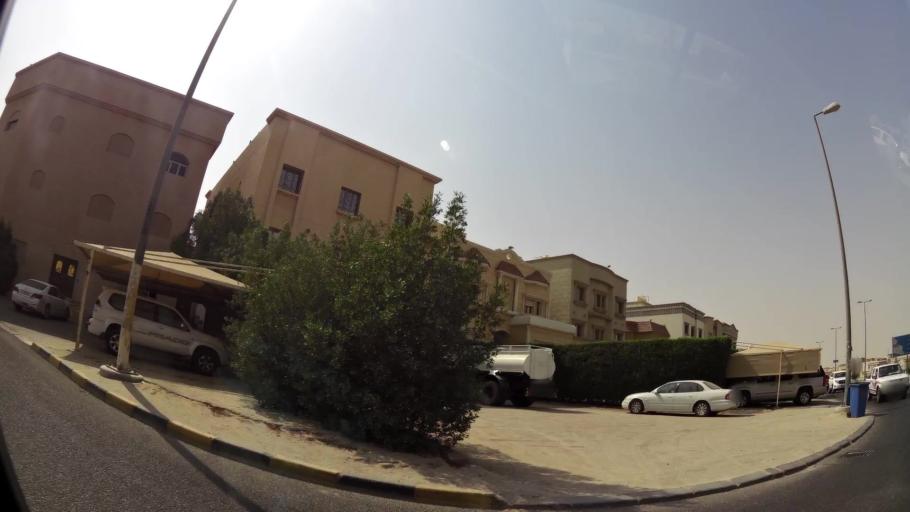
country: KW
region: Muhafazat al Jahra'
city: Al Jahra'
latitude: 29.3067
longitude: 47.7112
